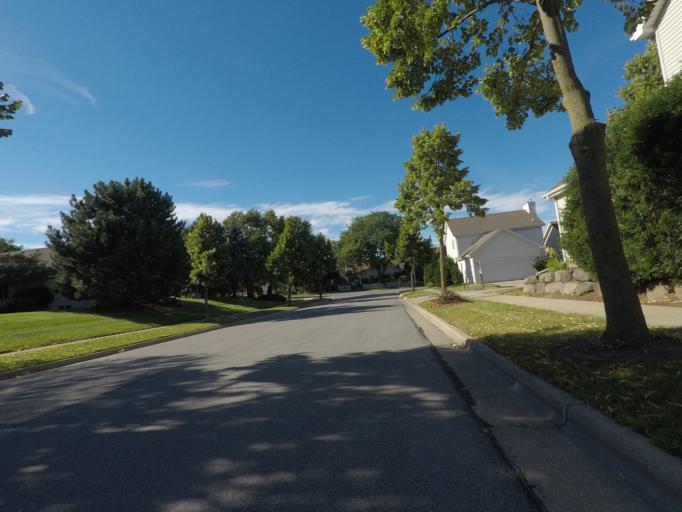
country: US
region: Wisconsin
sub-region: Dane County
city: Middleton
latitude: 43.0703
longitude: -89.5267
